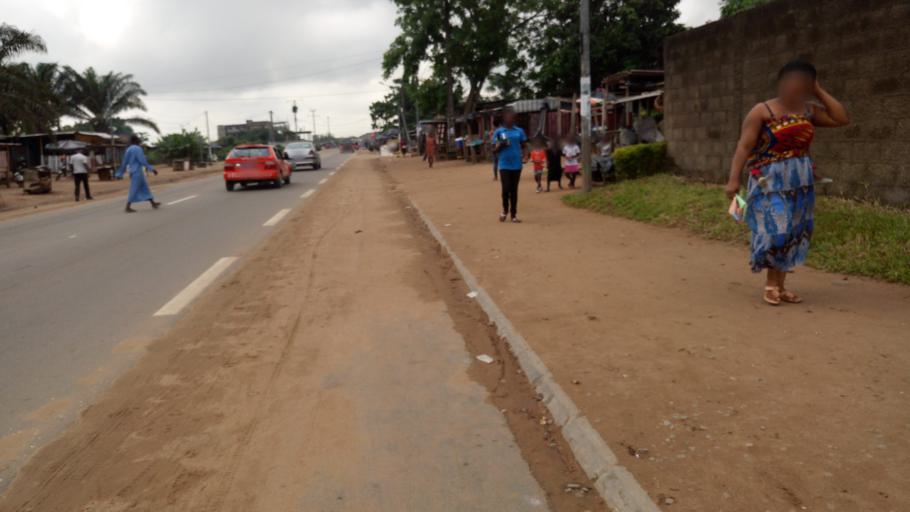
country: CI
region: Lagunes
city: Abobo
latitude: 5.4119
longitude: -3.9969
